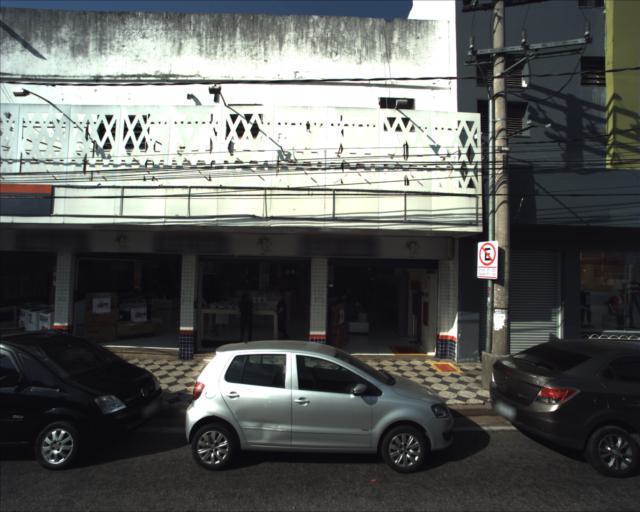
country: BR
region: Sao Paulo
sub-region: Sorocaba
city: Sorocaba
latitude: -23.4982
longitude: -47.4589
